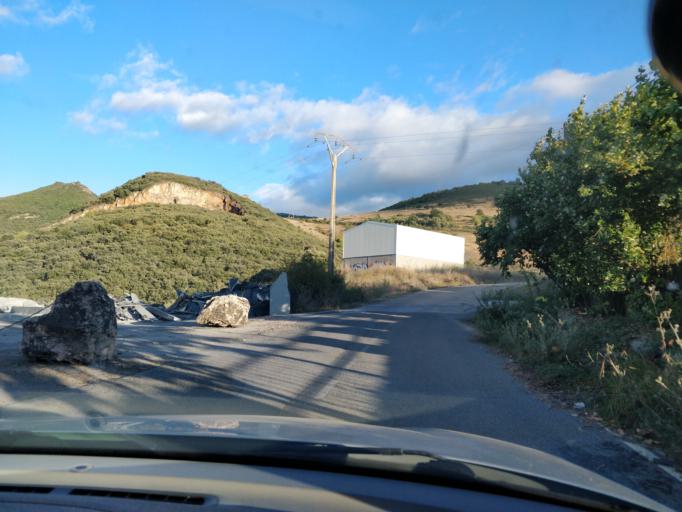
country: ES
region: Castille and Leon
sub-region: Provincia de Leon
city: Borrenes
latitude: 42.4912
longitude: -6.7023
